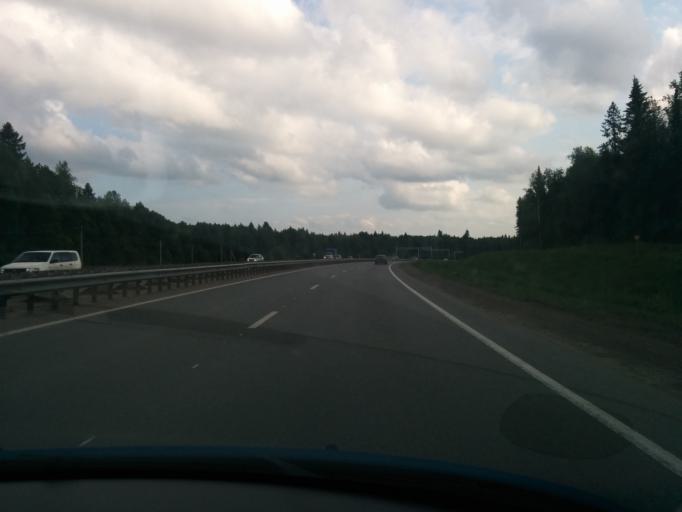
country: RU
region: Perm
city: Novyye Lyady
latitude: 58.0351
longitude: 56.4340
